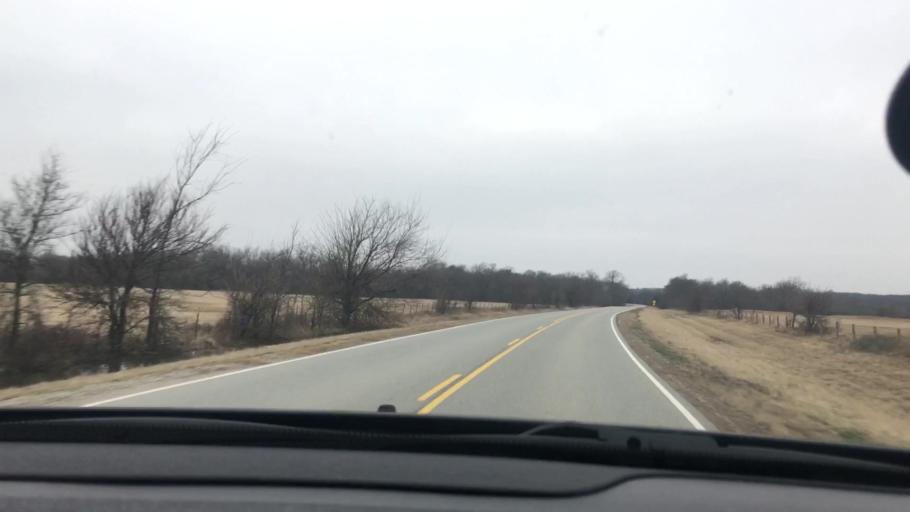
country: US
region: Oklahoma
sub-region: Coal County
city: Coalgate
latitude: 34.5318
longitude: -96.2552
